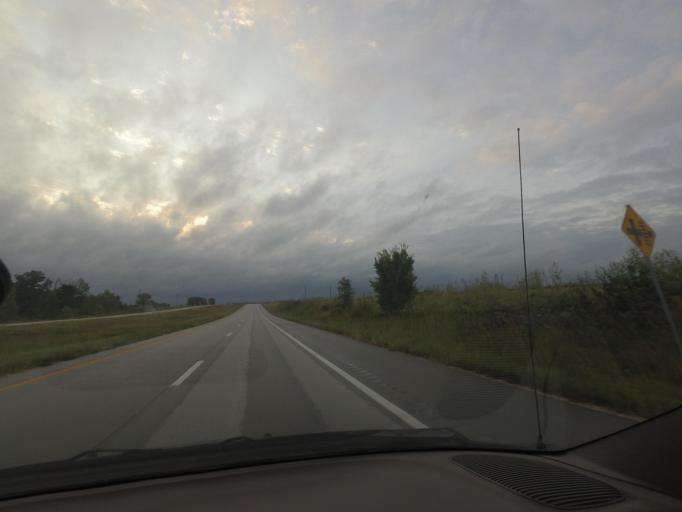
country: US
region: Missouri
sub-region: Shelby County
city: Shelbina
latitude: 39.6788
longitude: -91.9763
